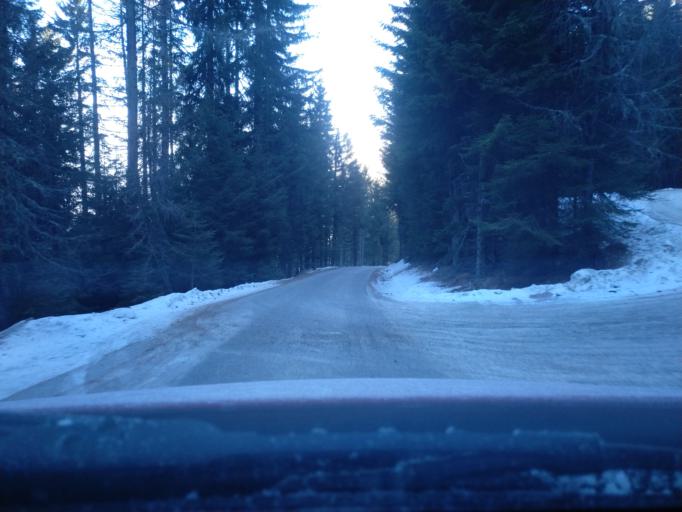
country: AT
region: Carinthia
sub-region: Politischer Bezirk Villach Land
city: Arriach
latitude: 46.7059
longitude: 13.9010
